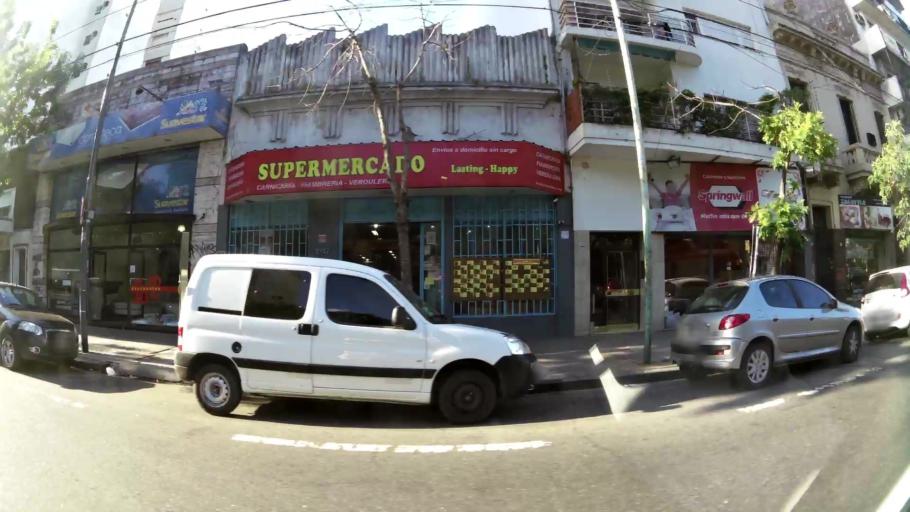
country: AR
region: Buenos Aires F.D.
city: Buenos Aires
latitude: -34.6149
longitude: -58.4066
